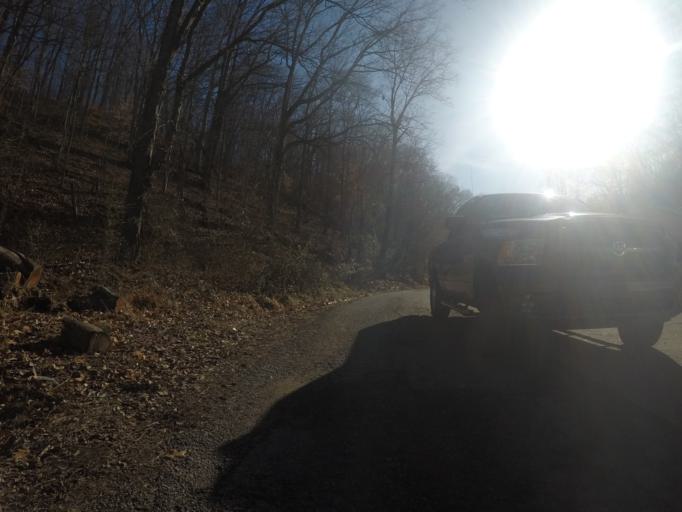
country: US
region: Ohio
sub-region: Lawrence County
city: Burlington
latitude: 38.3933
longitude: -82.4977
